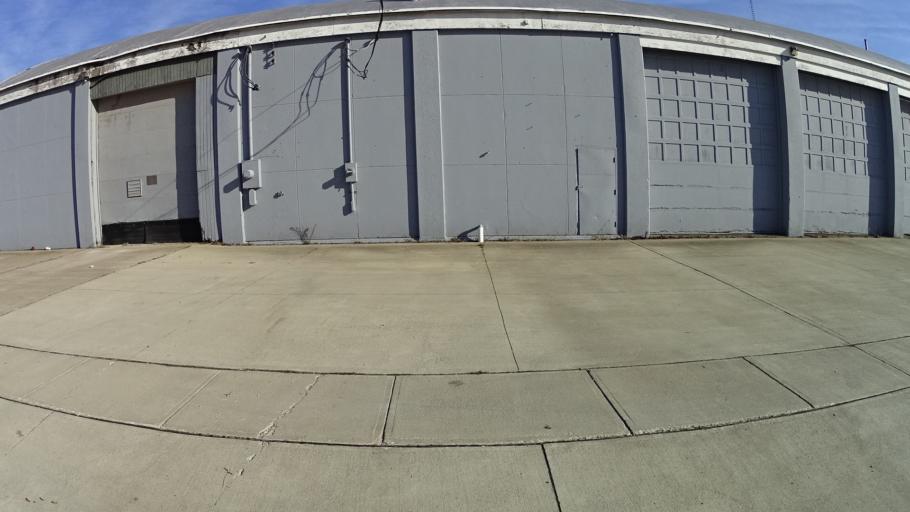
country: US
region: Ohio
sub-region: Lorain County
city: Elyria
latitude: 41.3743
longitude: -82.1229
